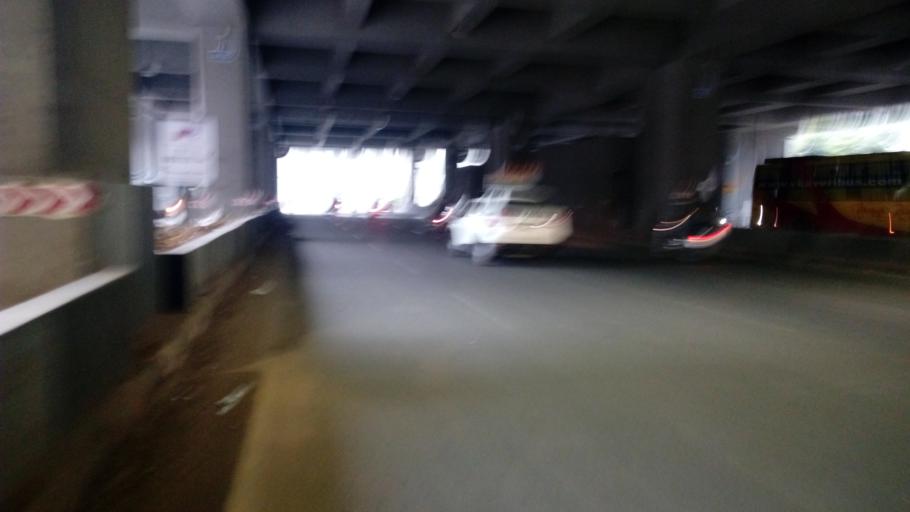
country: IN
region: Telangana
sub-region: Hyderabad
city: Hyderabad
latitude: 17.4357
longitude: 78.4447
